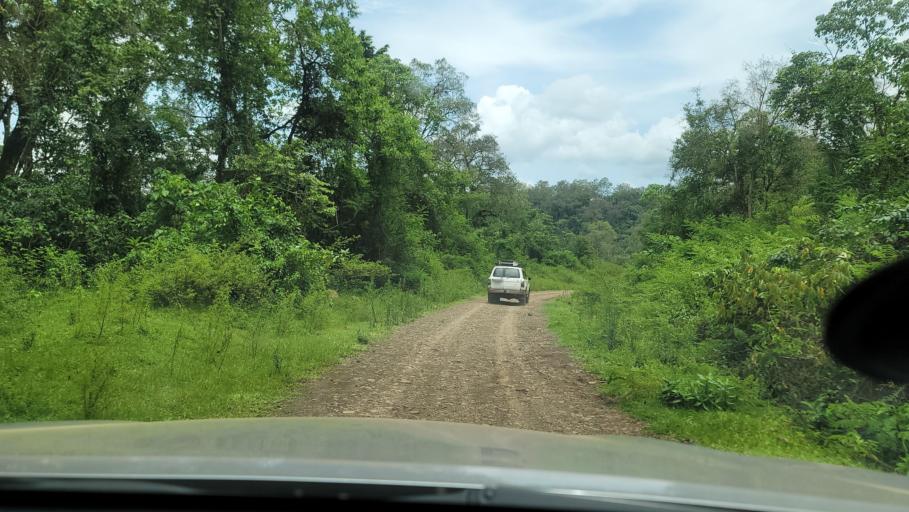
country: ET
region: Southern Nations, Nationalities, and People's Region
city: Bonga
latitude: 7.6379
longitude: 36.2310
